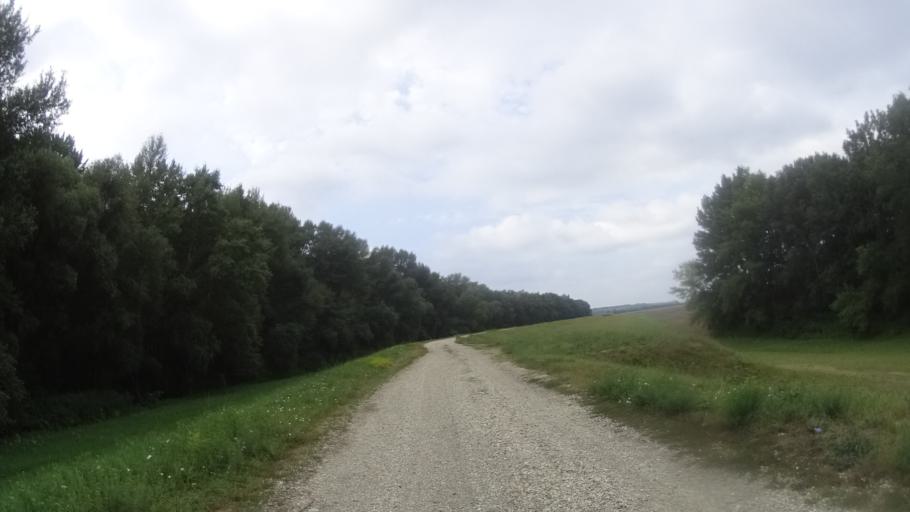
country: HU
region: Gyor-Moson-Sopron
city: Bony
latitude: 47.7483
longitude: 17.9097
